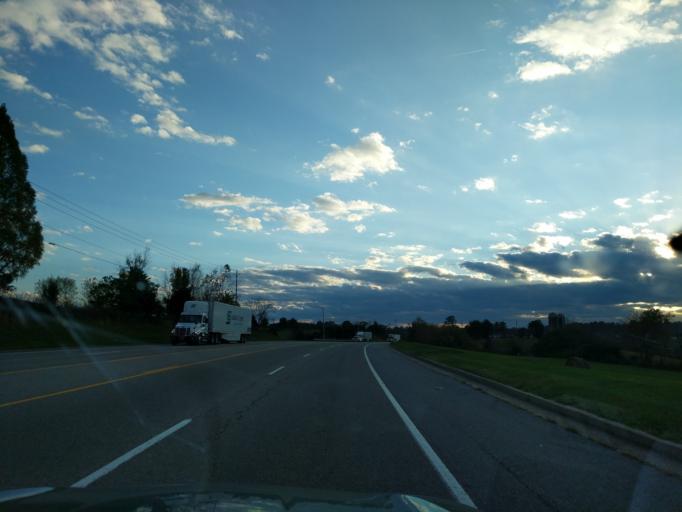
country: US
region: Tennessee
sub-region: Washington County
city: Spurgeon
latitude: 36.4280
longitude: -82.4568
